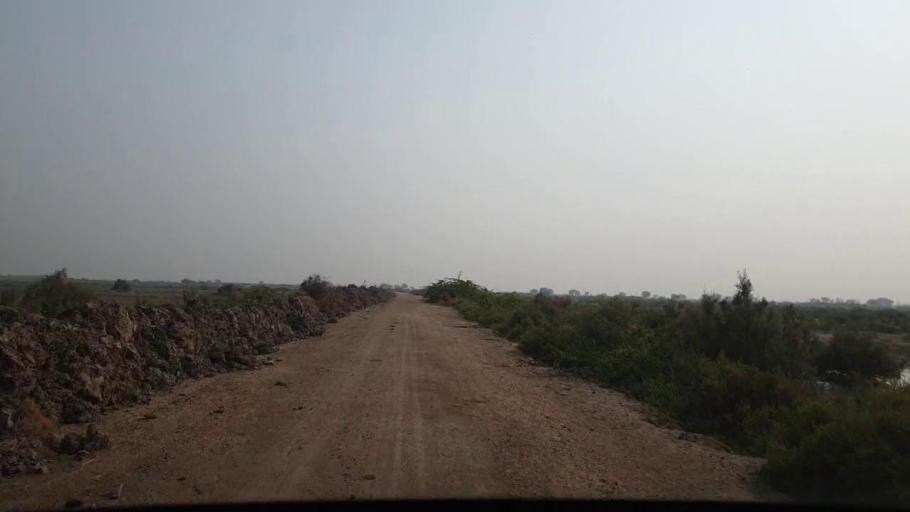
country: PK
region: Sindh
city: Jati
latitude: 24.2831
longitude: 68.4171
